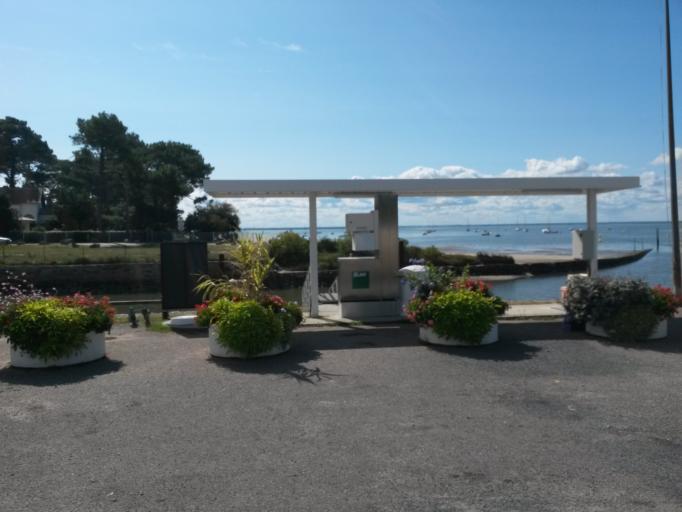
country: FR
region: Aquitaine
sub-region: Departement de la Gironde
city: Andernos-les-Bains
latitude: 44.7226
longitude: -1.0770
